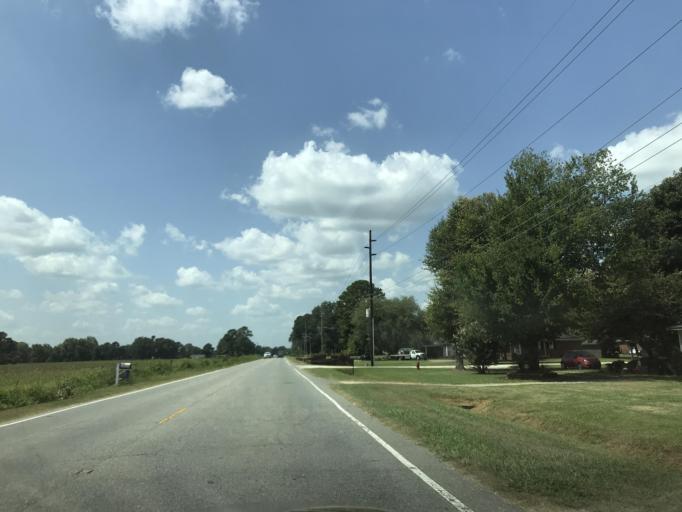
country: US
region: North Carolina
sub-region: Sampson County
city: Plain View
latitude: 35.2470
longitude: -78.3606
